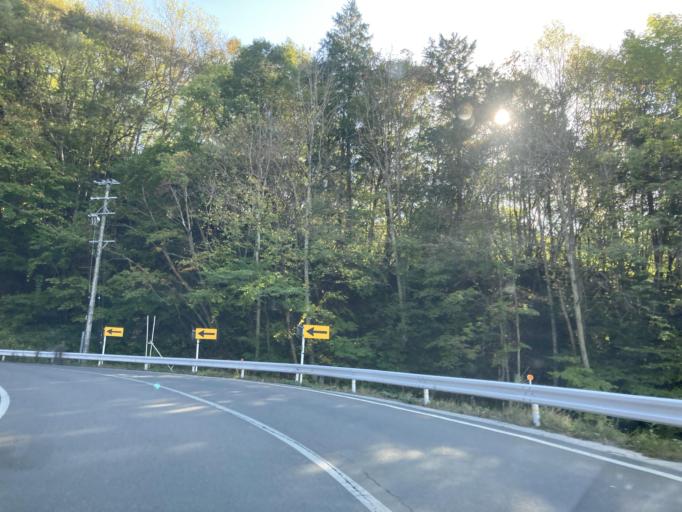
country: JP
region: Nagano
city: Omachi
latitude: 36.4853
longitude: 137.8857
